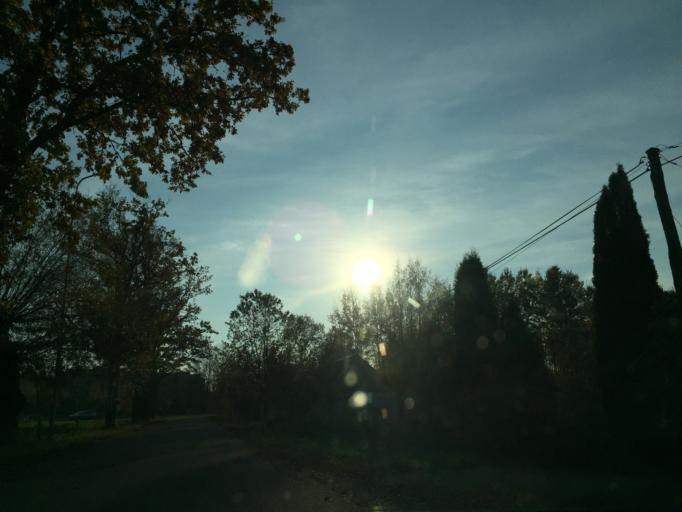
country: LV
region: Skrunda
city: Skrunda
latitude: 56.6740
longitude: 22.0020
